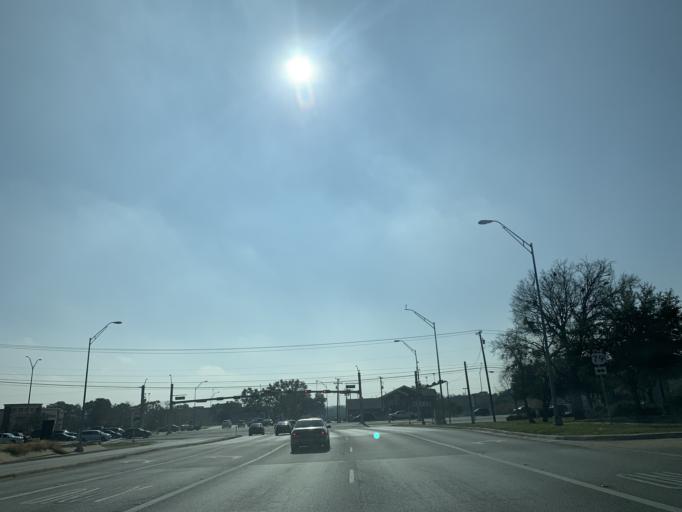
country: US
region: Texas
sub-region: Williamson County
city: Round Rock
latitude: 30.5190
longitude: -97.6557
